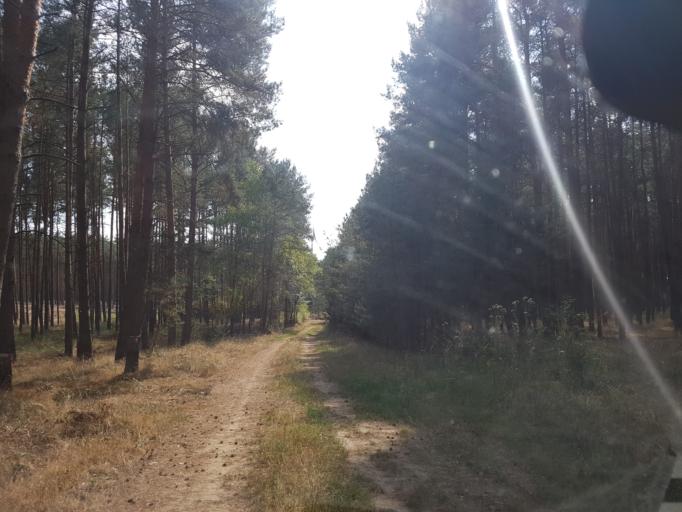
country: DE
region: Brandenburg
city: Treuenbrietzen
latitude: 52.0248
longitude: 12.8809
